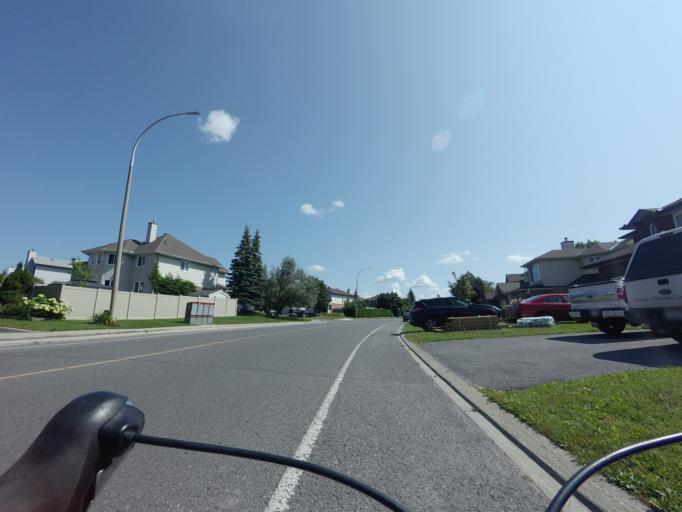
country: CA
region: Ontario
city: Bells Corners
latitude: 45.2853
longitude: -75.8540
